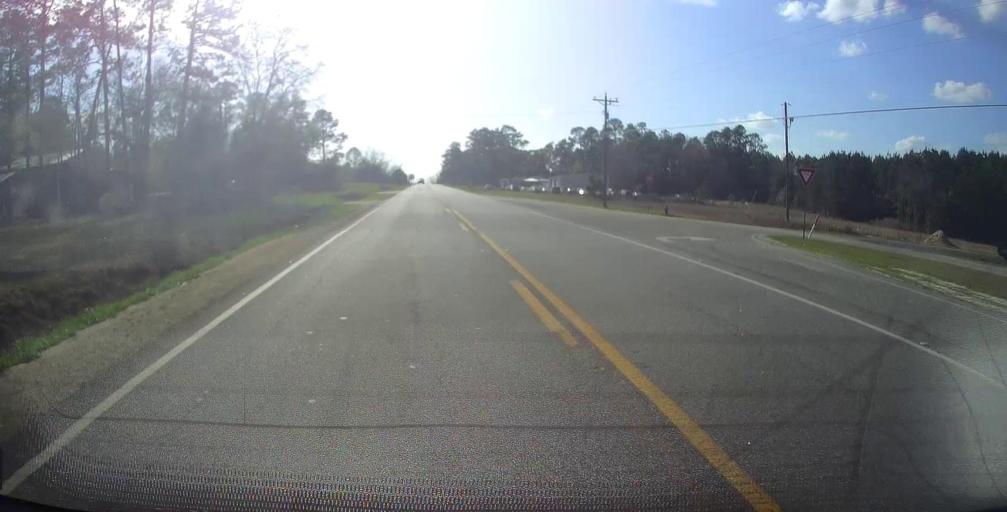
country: US
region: Georgia
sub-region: Wheeler County
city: Alamo
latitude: 32.1528
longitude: -82.7657
